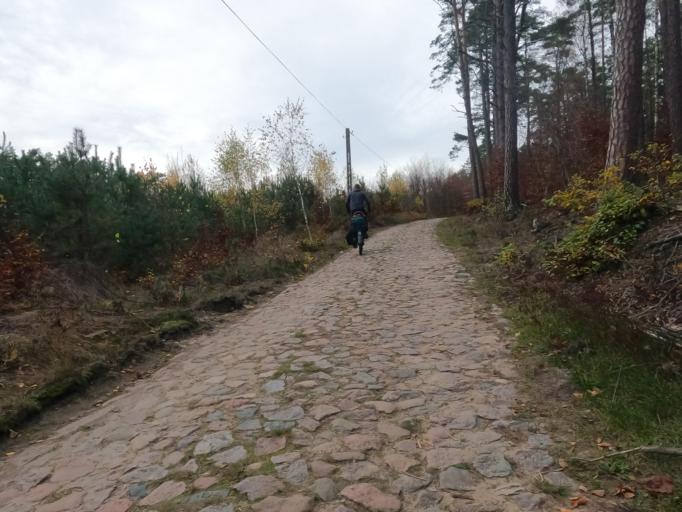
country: PL
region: Pomeranian Voivodeship
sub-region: Powiat starogardzki
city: Skarszewy
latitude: 54.0460
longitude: 18.4555
